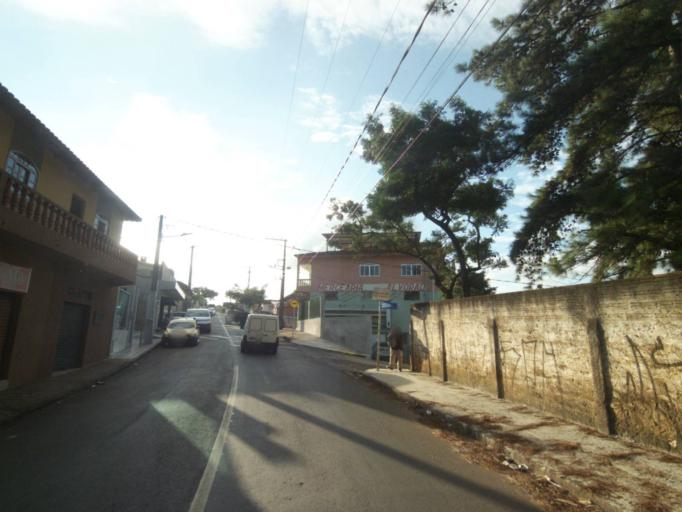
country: BR
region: Parana
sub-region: Telemaco Borba
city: Telemaco Borba
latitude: -24.3269
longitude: -50.6351
